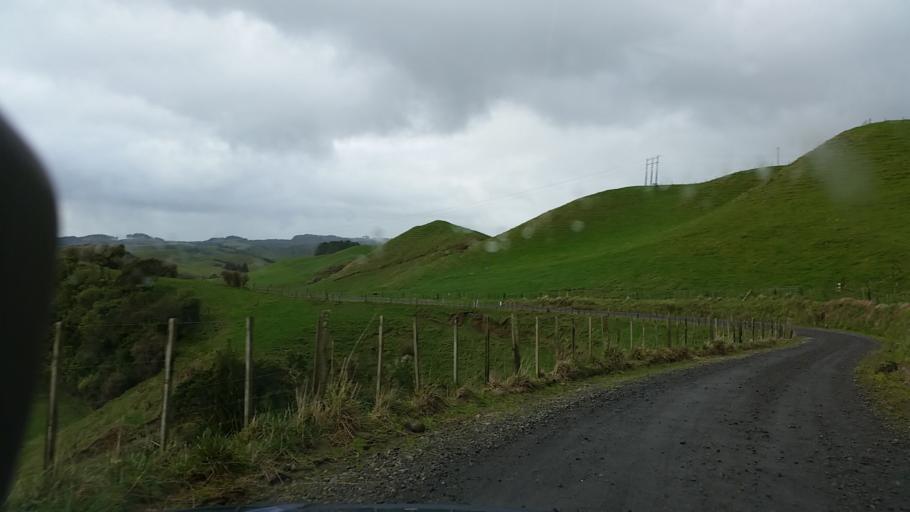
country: NZ
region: Taranaki
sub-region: South Taranaki District
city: Eltham
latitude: -39.2805
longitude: 174.3361
